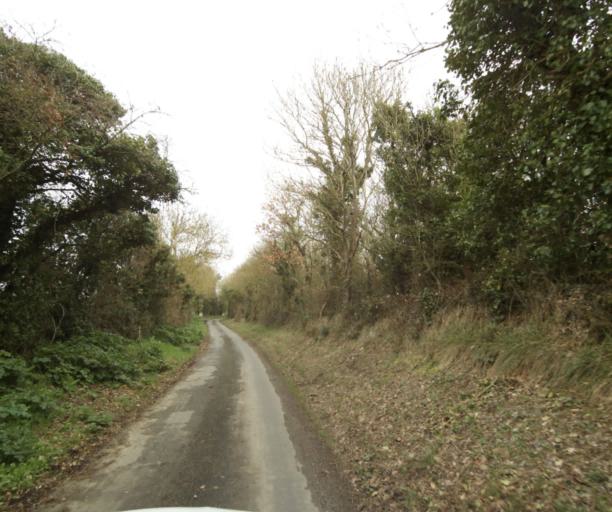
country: FR
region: Poitou-Charentes
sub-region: Departement de la Charente-Maritime
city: Nieul-sur-Mer
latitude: 46.1872
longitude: -1.1769
